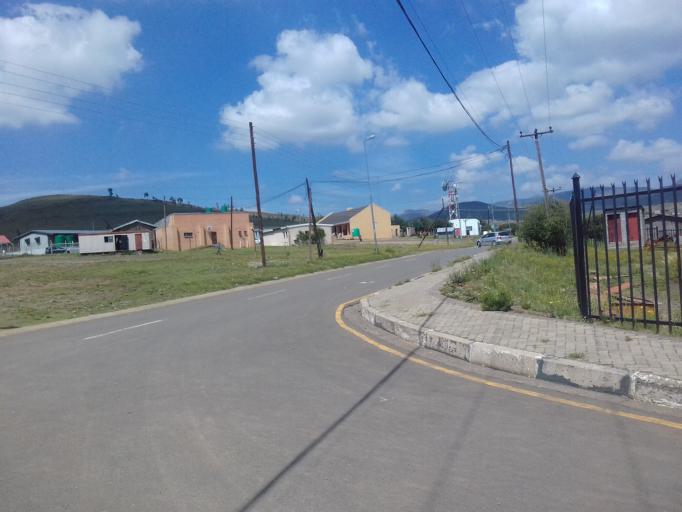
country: LS
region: Thaba-Tseka
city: Thaba-Tseka
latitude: -29.5213
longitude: 28.6079
